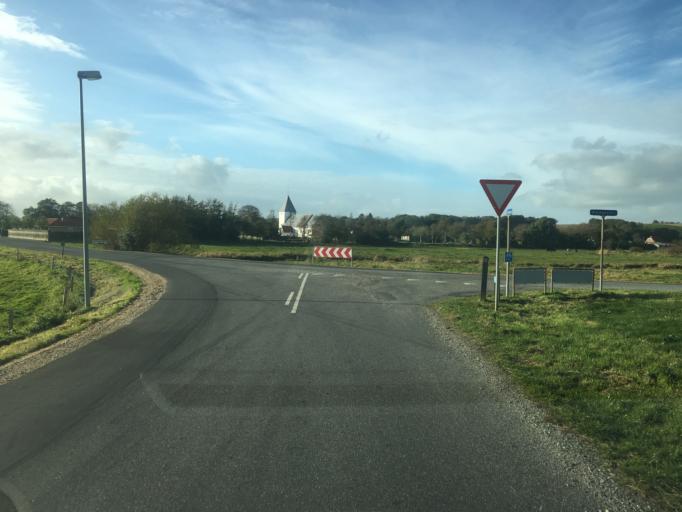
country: DK
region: South Denmark
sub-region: Tonder Kommune
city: Logumkloster
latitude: 55.0753
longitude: 8.9357
